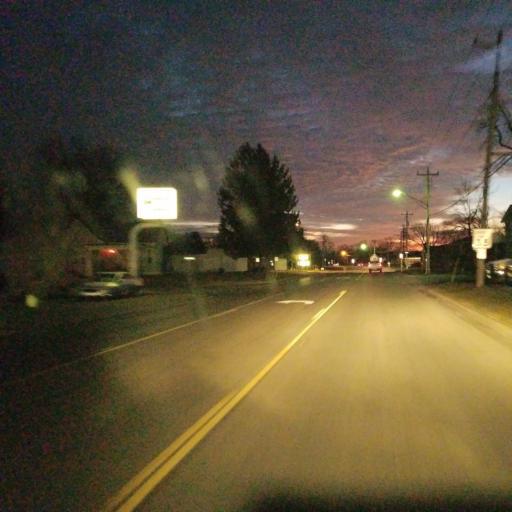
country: US
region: Illinois
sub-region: Peoria County
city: Hanna City
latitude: 40.6919
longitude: -89.7945
